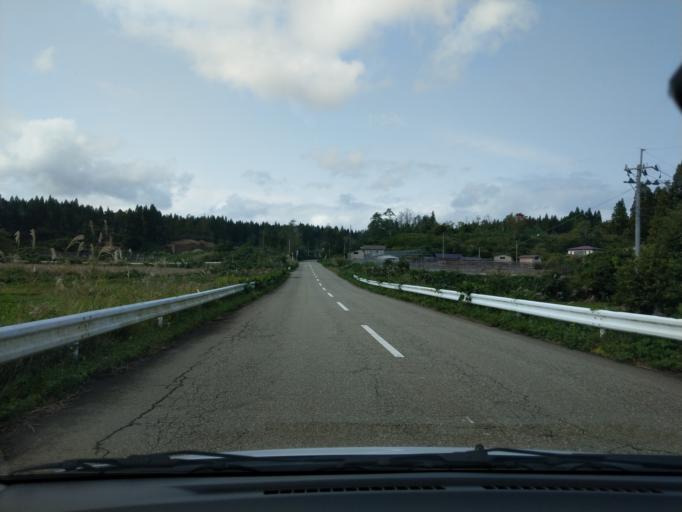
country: JP
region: Akita
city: Omagari
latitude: 39.5195
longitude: 140.3016
